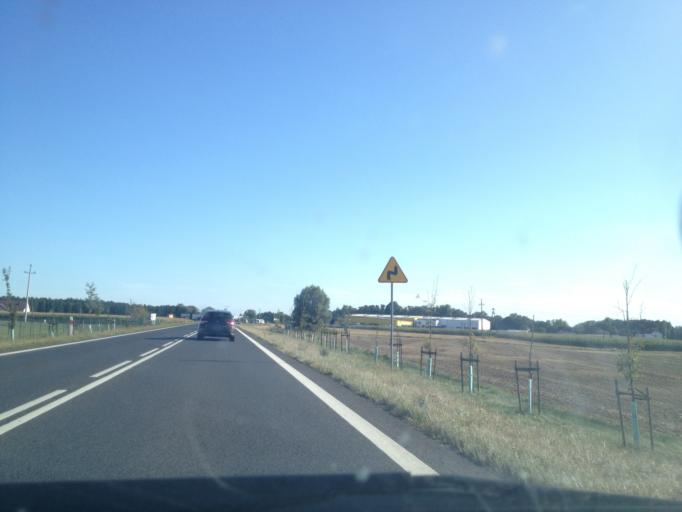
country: PL
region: Greater Poland Voivodeship
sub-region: Powiat sremski
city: Srem
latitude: 52.1115
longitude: 17.0435
